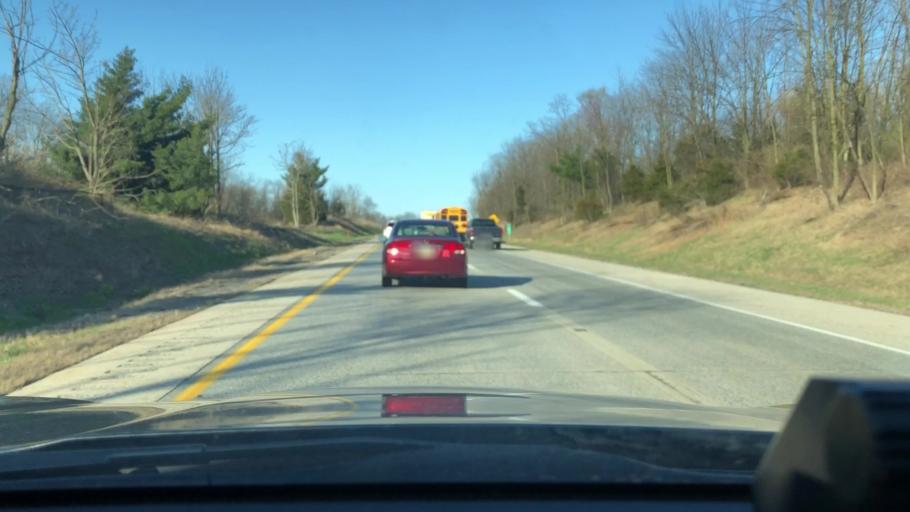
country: US
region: Pennsylvania
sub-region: Lebanon County
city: Jonestown
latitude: 40.4375
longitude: -76.4878
